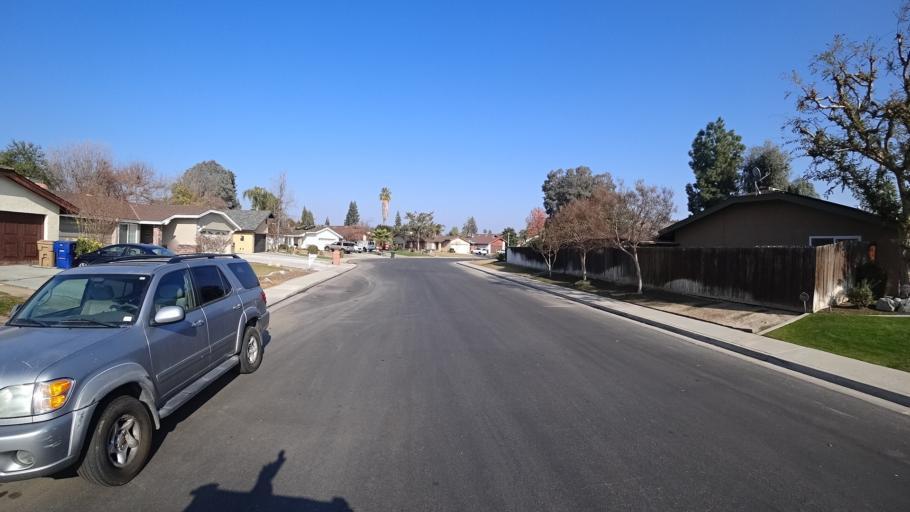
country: US
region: California
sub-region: Kern County
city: Greenacres
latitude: 35.3208
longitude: -119.0852
